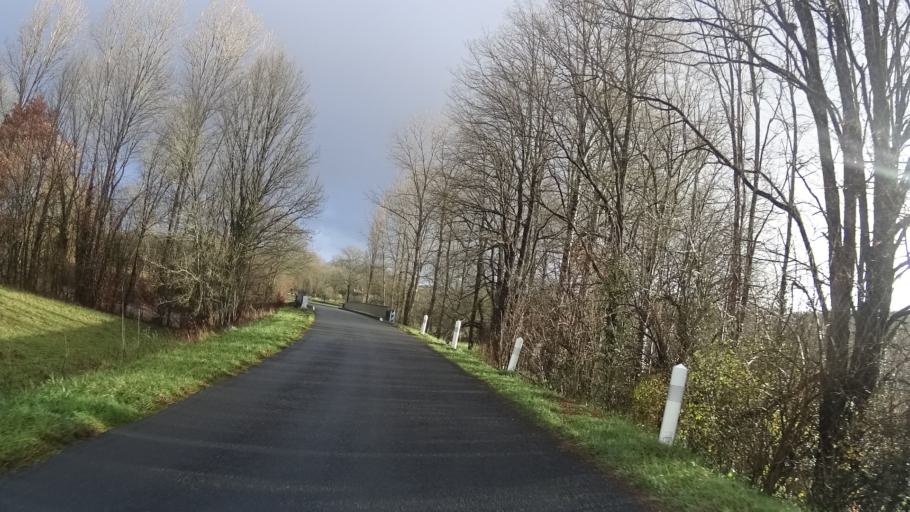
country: FR
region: Aquitaine
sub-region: Departement de la Dordogne
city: Sorges
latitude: 45.2751
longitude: 0.9384
